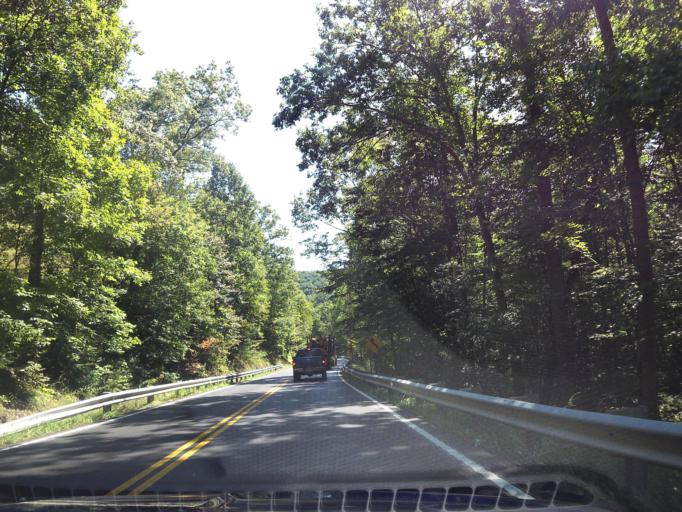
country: US
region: Kentucky
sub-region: Leslie County
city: Hyden
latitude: 37.1309
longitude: -83.4612
